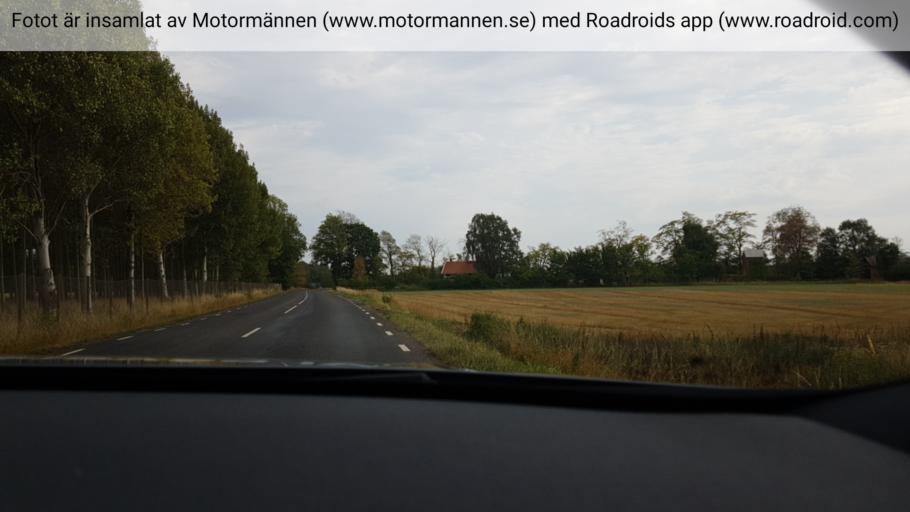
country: SE
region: Vaestra Goetaland
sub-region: Falkopings Kommun
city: Akarp
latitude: 58.1839
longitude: 13.6311
